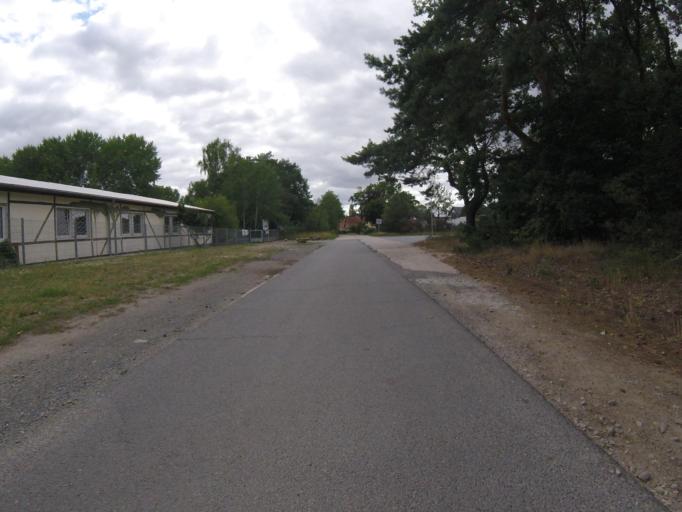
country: DE
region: Brandenburg
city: Konigs Wusterhausen
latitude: 52.3035
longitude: 13.6623
